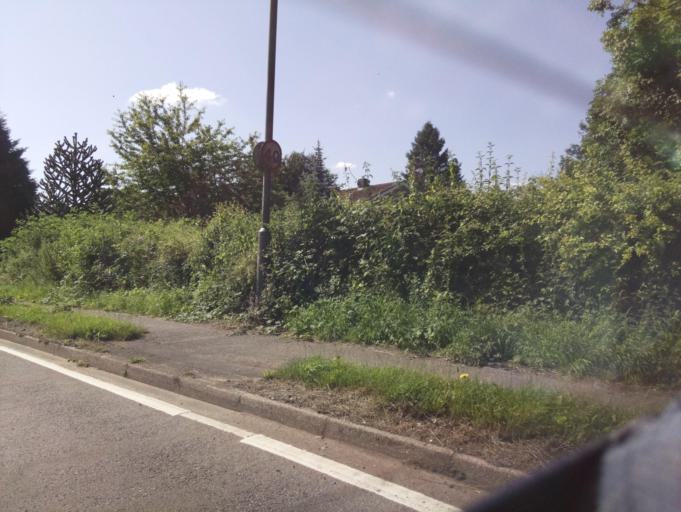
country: GB
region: England
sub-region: Derbyshire
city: Duffield
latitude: 52.9789
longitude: -1.4858
